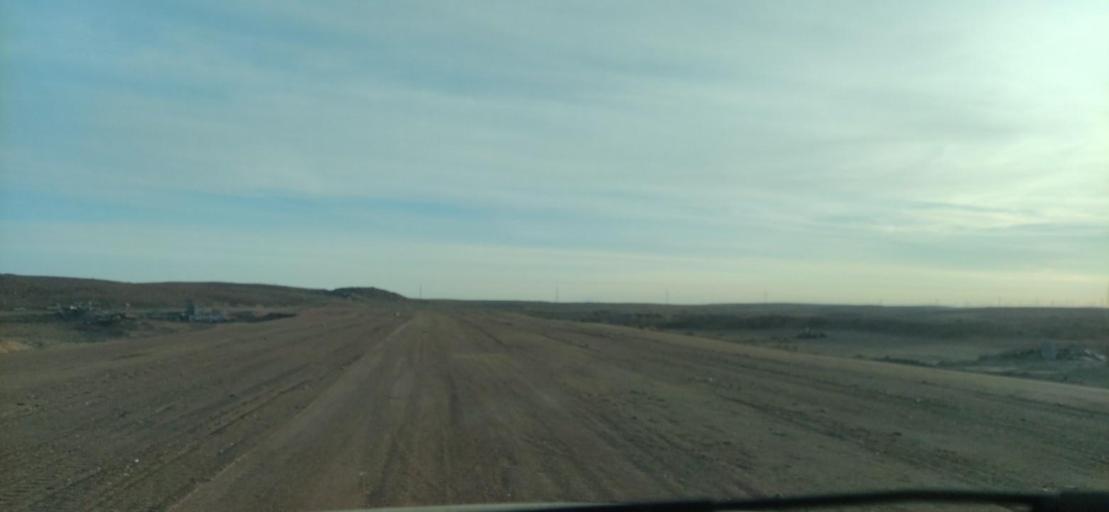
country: KZ
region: Qaraghandy
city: Saryshaghan
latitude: 46.1121
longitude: 73.5955
